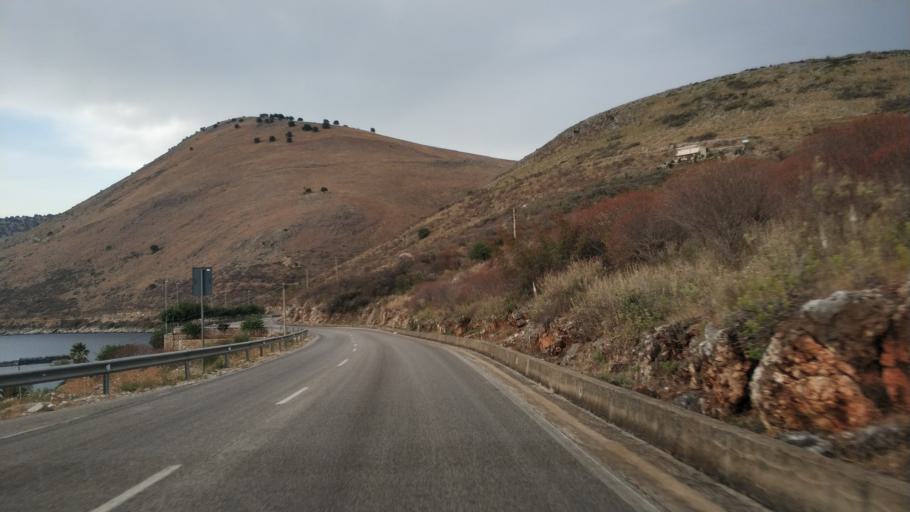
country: AL
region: Vlore
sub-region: Rrethi i Vlores
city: Himare
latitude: 40.0514
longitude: 19.8037
